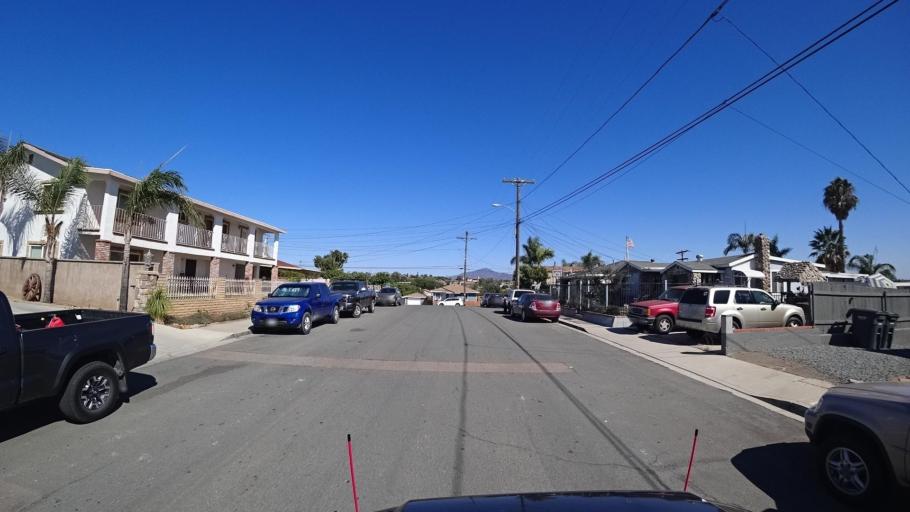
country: US
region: California
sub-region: San Diego County
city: National City
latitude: 32.6699
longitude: -117.0712
